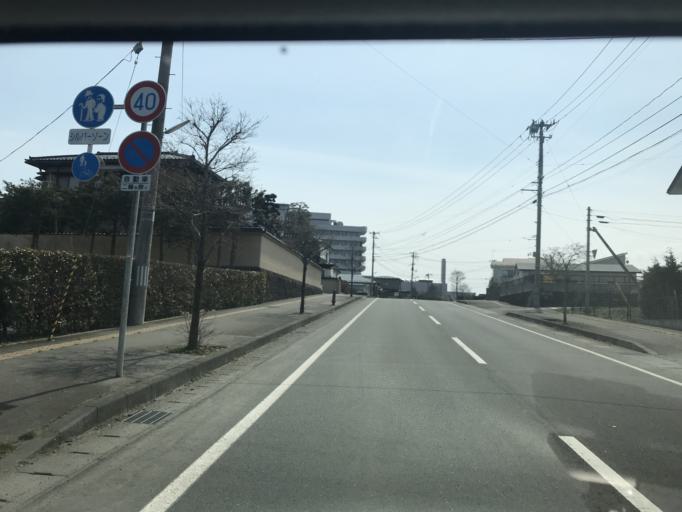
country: JP
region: Iwate
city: Mizusawa
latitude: 39.1249
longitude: 141.1349
